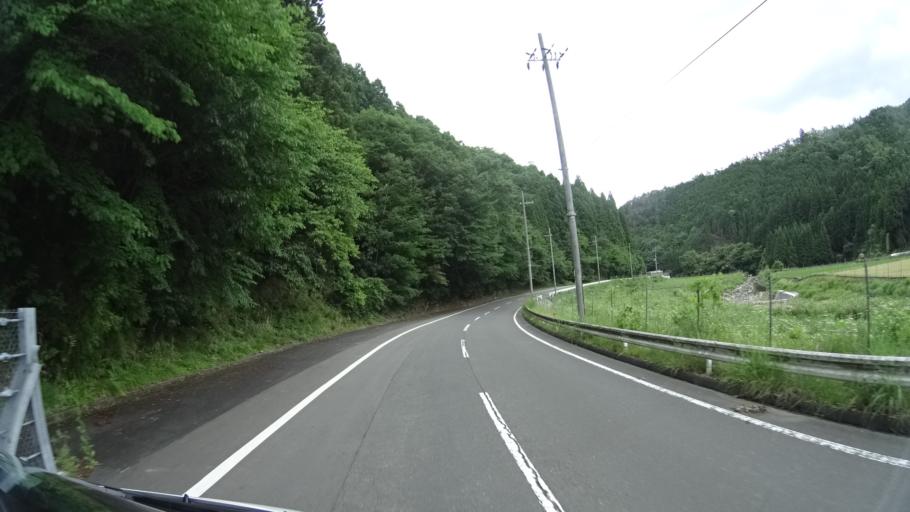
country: JP
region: Hyogo
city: Sasayama
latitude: 35.0582
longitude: 135.3921
